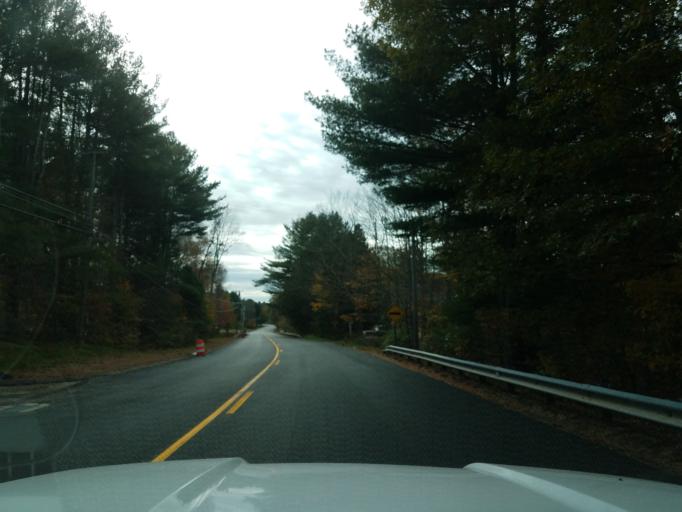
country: US
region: Connecticut
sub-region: Tolland County
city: Storrs
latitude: 41.8696
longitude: -72.1608
